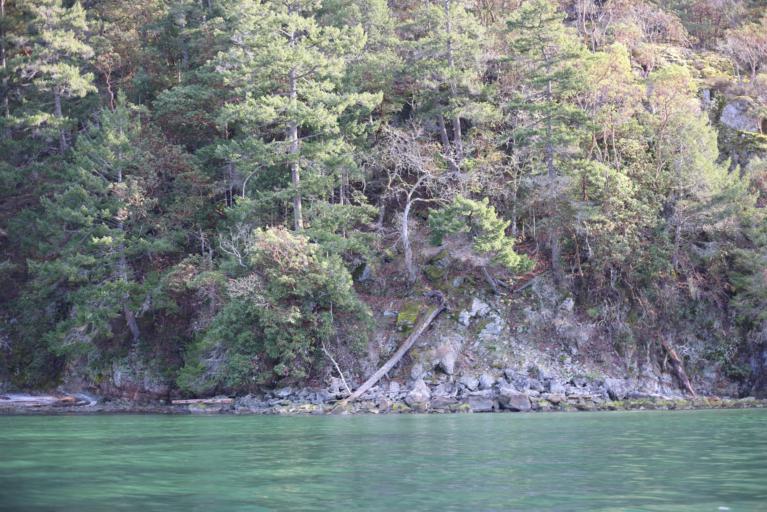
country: CA
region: British Columbia
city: Duncan
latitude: 48.7573
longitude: -123.5911
